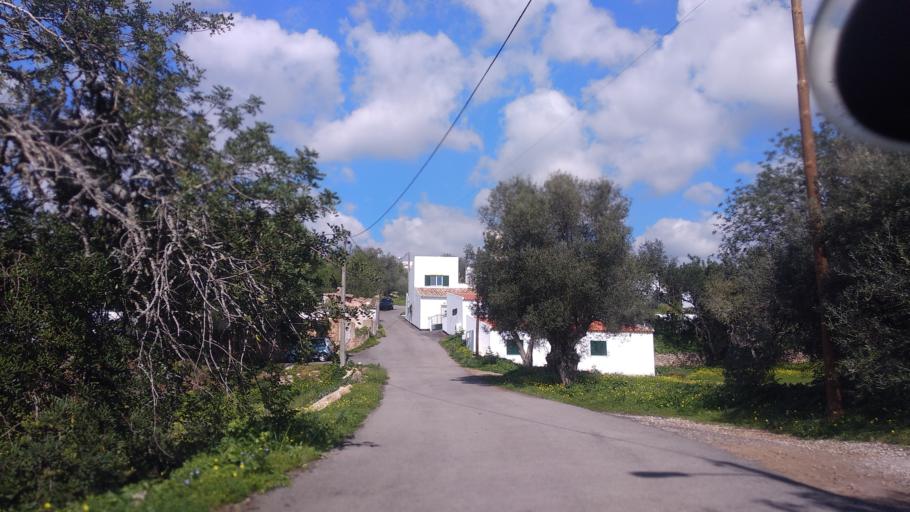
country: PT
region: Faro
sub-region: Sao Bras de Alportel
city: Sao Bras de Alportel
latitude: 37.1483
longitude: -7.8854
